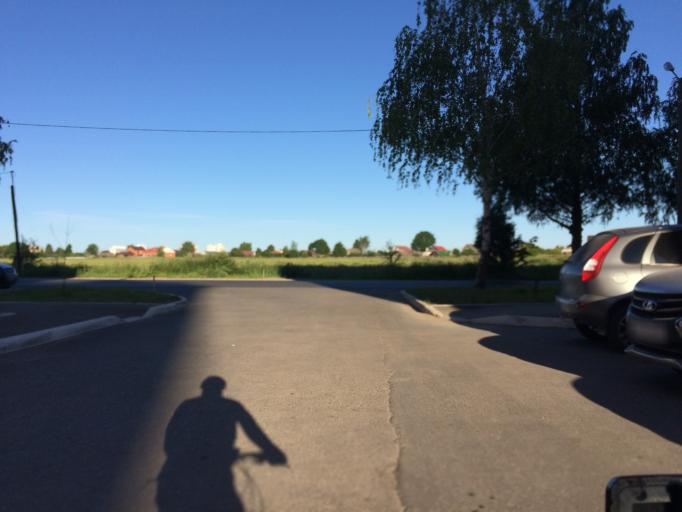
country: RU
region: Mariy-El
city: Medvedevo
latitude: 56.6466
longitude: 47.8315
